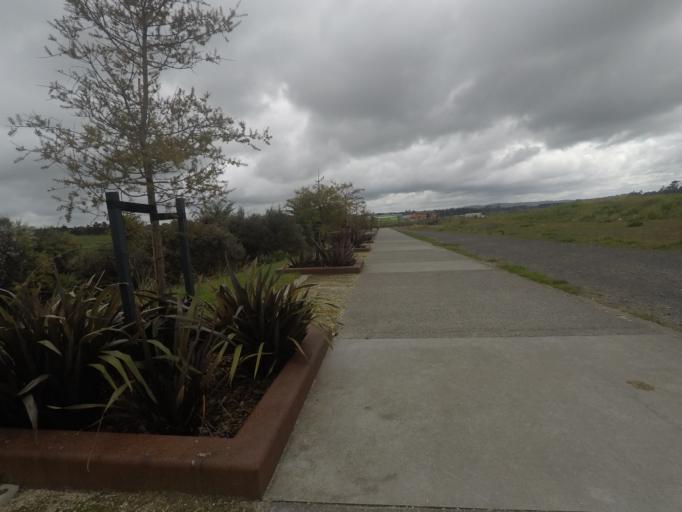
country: NZ
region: Auckland
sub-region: Auckland
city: Rosebank
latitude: -36.8154
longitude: 174.6078
